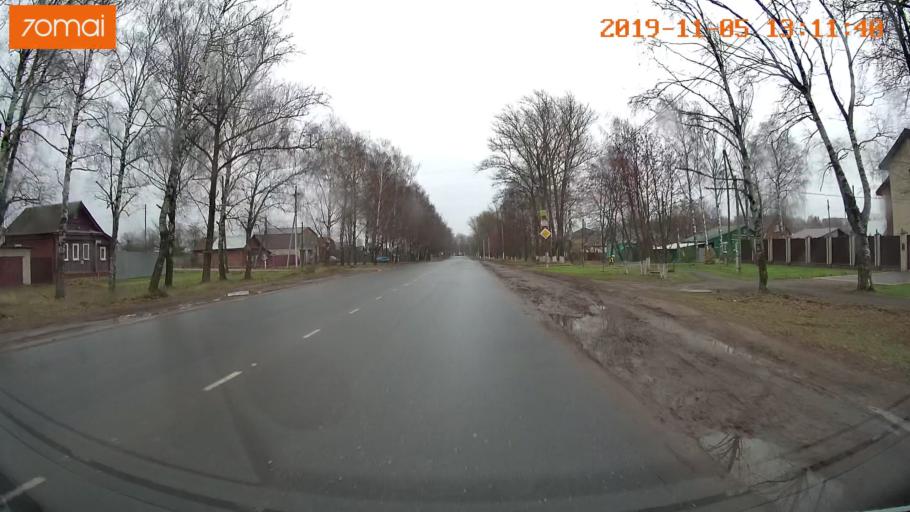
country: RU
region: Ivanovo
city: Shuya
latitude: 56.8584
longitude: 41.3425
